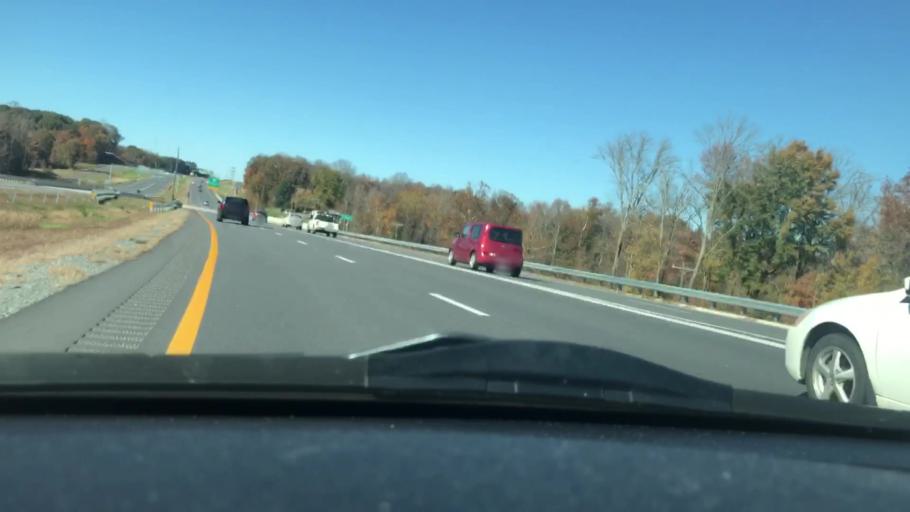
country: US
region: North Carolina
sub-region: Guilford County
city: Summerfield
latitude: 36.2270
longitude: -79.9133
